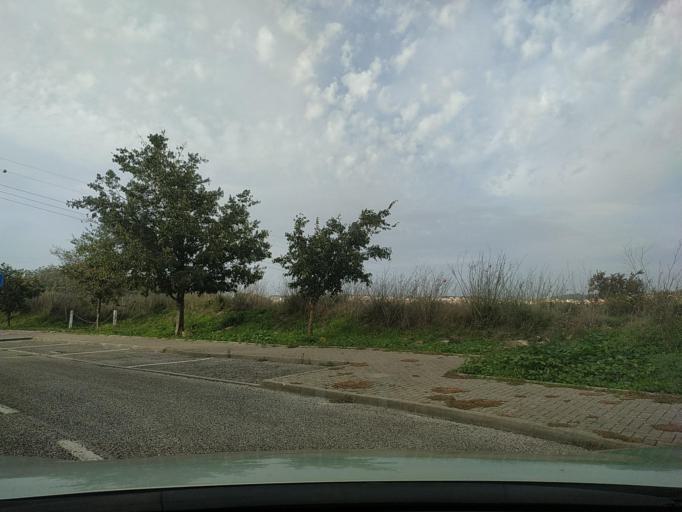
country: PT
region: Lisbon
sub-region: Odivelas
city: Famoes
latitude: 38.7857
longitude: -9.2293
